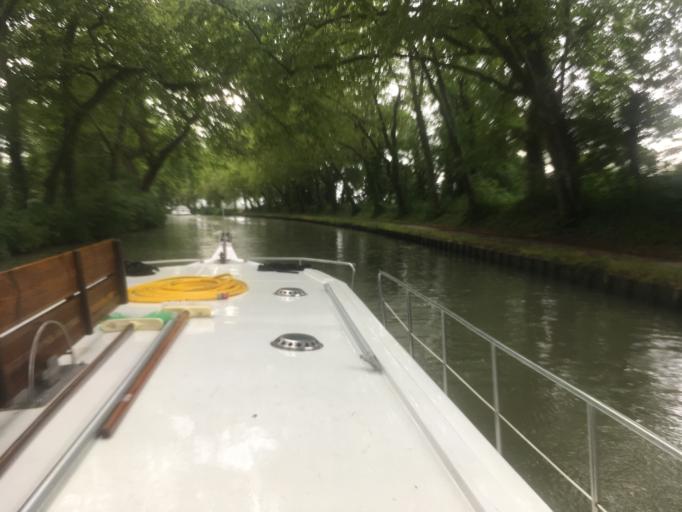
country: FR
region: Midi-Pyrenees
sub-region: Departement de la Haute-Garonne
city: Avignonet-Lauragais
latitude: 43.3576
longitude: 1.8133
